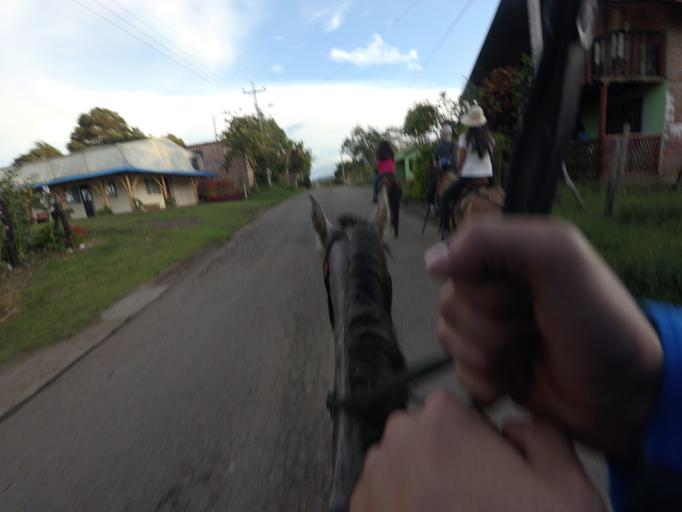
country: CO
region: Huila
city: San Agustin
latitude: 1.8921
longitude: -76.2723
